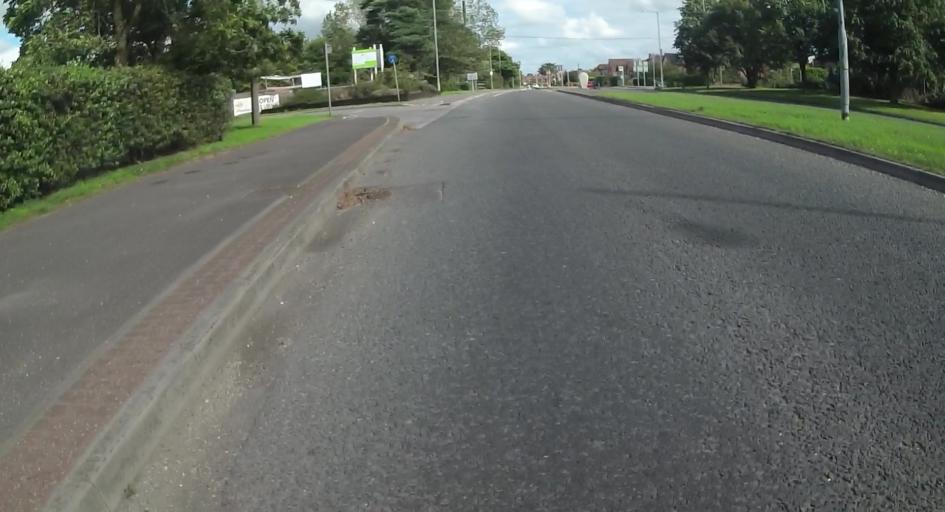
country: GB
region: England
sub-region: West Berkshire
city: Thatcham
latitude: 51.4062
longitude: -1.2839
